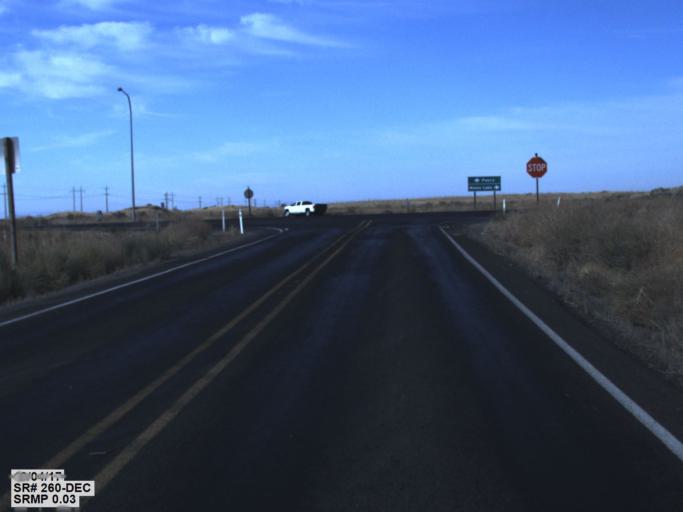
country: US
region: Washington
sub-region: Franklin County
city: Connell
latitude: 46.6650
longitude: -119.0056
